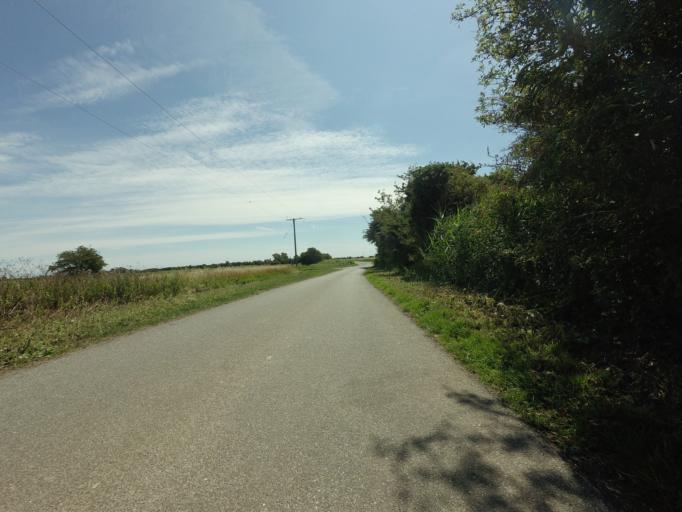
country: GB
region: England
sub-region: Kent
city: Lydd
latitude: 50.9796
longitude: 0.8466
